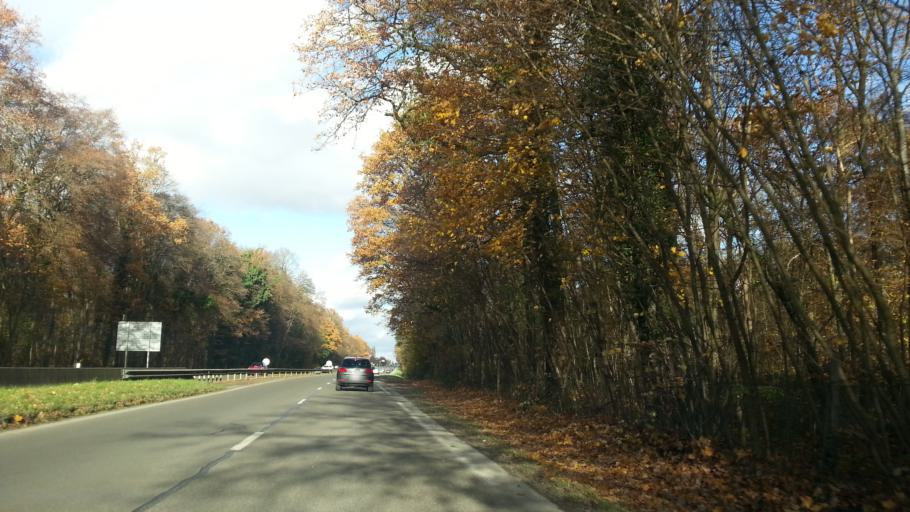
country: FR
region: Picardie
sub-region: Departement de l'Oise
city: Saint-Maximin
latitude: 49.2226
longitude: 2.4678
